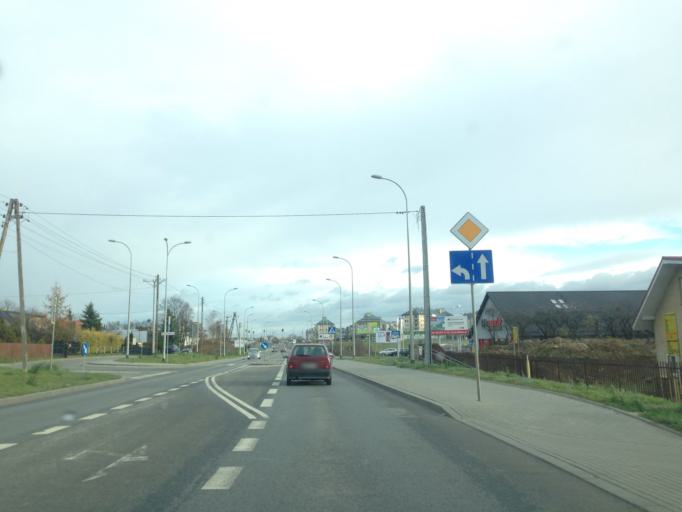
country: PL
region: Pomeranian Voivodeship
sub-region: Powiat gdanski
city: Kowale
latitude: 54.3220
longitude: 18.6002
